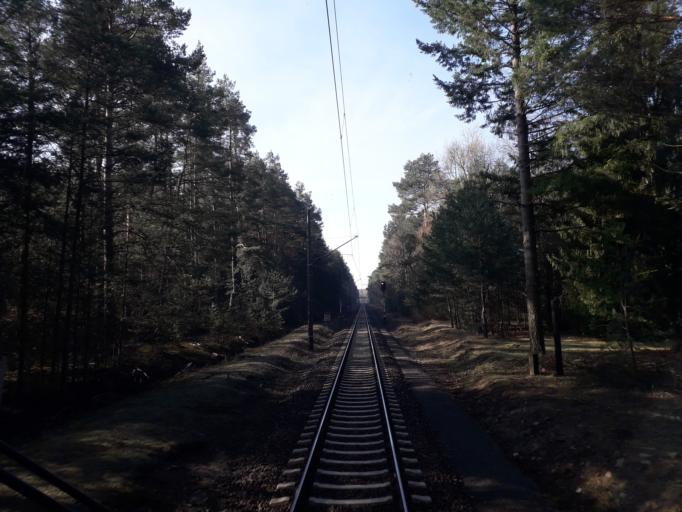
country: DE
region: Brandenburg
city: Beelitz
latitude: 52.2941
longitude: 12.9587
